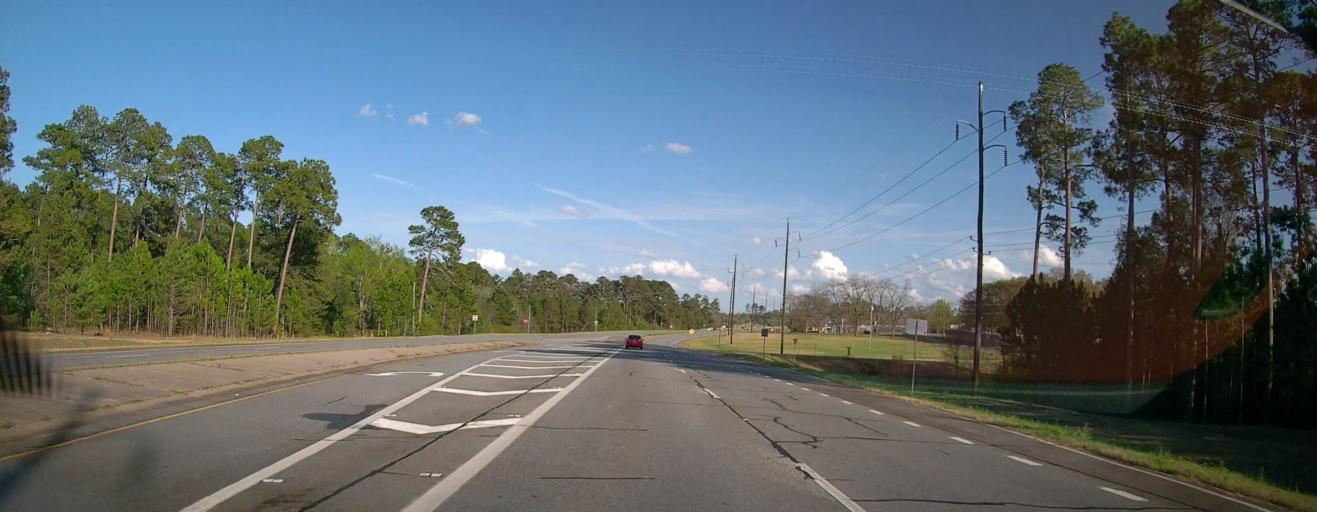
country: US
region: Georgia
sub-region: Baldwin County
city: Milledgeville
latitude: 33.0939
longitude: -83.2557
